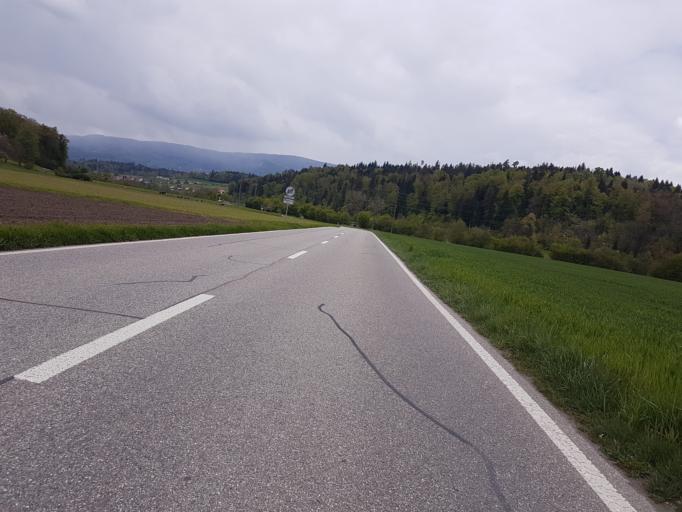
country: CH
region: Bern
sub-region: Oberaargau
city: Niederbipp
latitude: 47.2283
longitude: 7.7091
